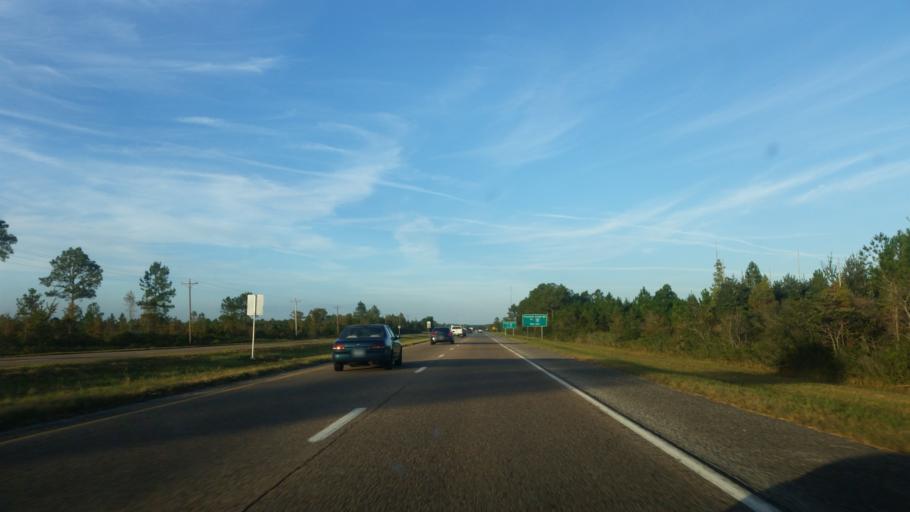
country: US
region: Alabama
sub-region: Mobile County
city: Grand Bay
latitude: 30.4533
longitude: -88.4215
